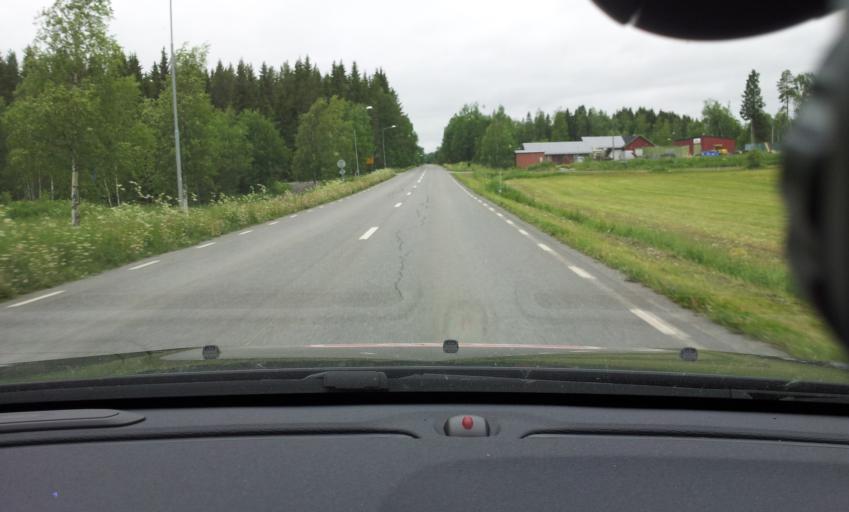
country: SE
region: Jaemtland
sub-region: Bergs Kommun
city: Hoverberg
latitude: 62.9991
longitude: 14.3520
